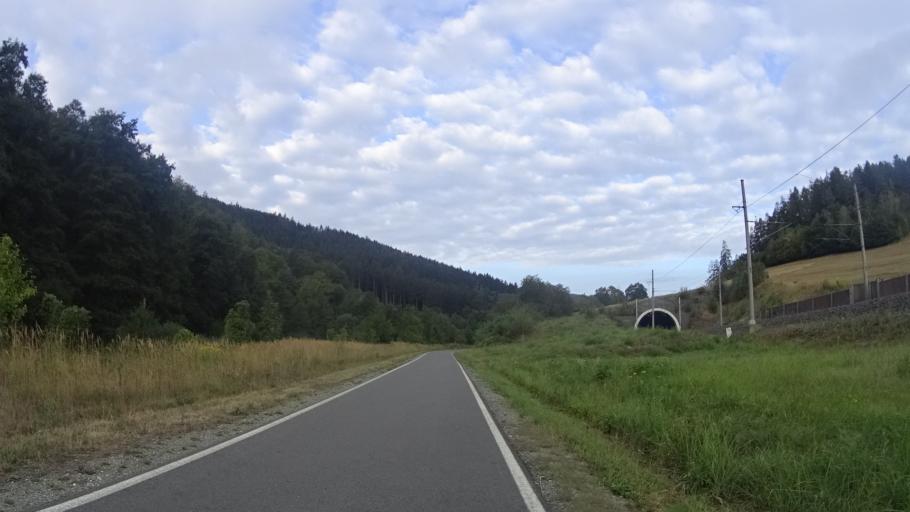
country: CZ
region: Olomoucky
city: Zabreh
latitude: 49.8634
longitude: 16.8142
